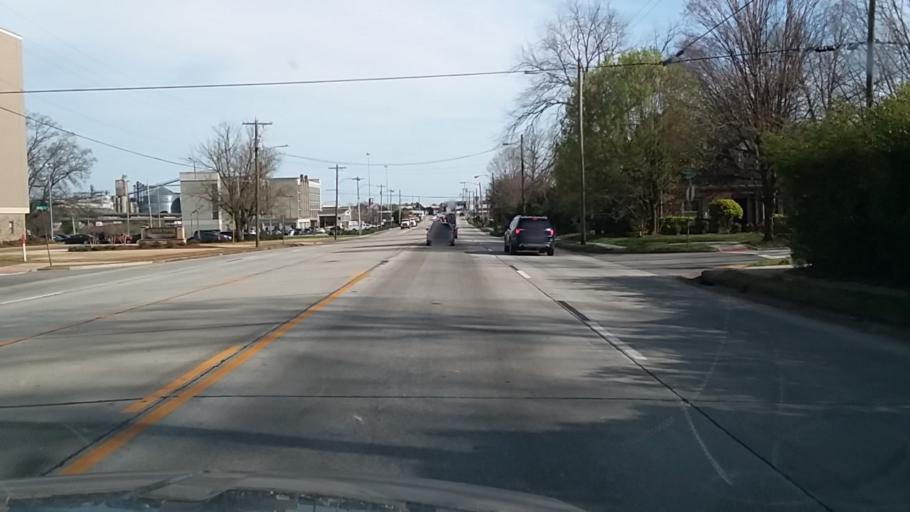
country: US
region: Alabama
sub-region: Morgan County
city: Decatur
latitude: 34.6121
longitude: -86.9805
